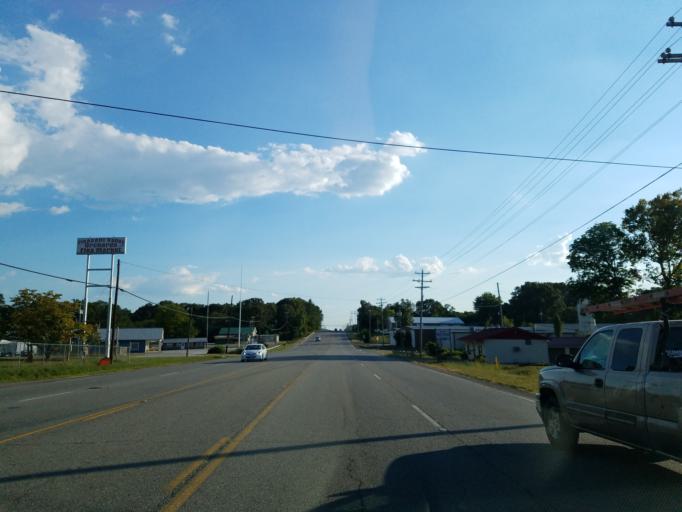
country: US
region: Georgia
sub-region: Murray County
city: Chatsworth
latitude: 34.8414
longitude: -84.7578
